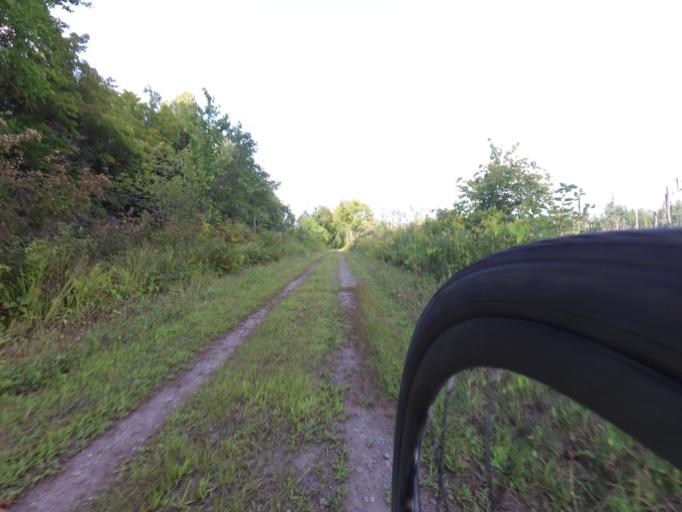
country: CA
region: Ontario
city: Kingston
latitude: 44.4792
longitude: -76.4820
